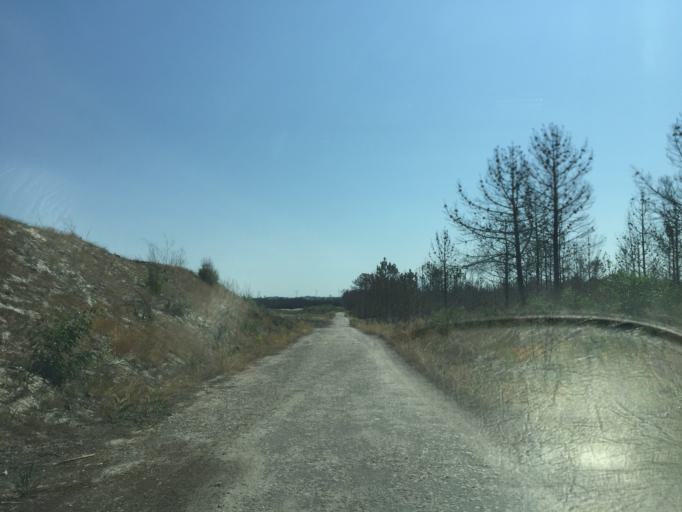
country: PT
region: Coimbra
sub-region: Figueira da Foz
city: Alhadas
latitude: 40.2607
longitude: -8.8346
